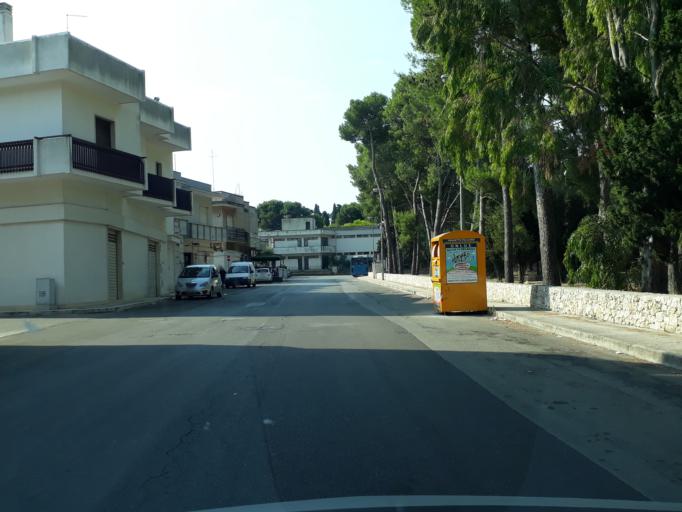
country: IT
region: Apulia
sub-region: Provincia di Brindisi
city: Carovigno
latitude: 40.7114
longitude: 17.6566
